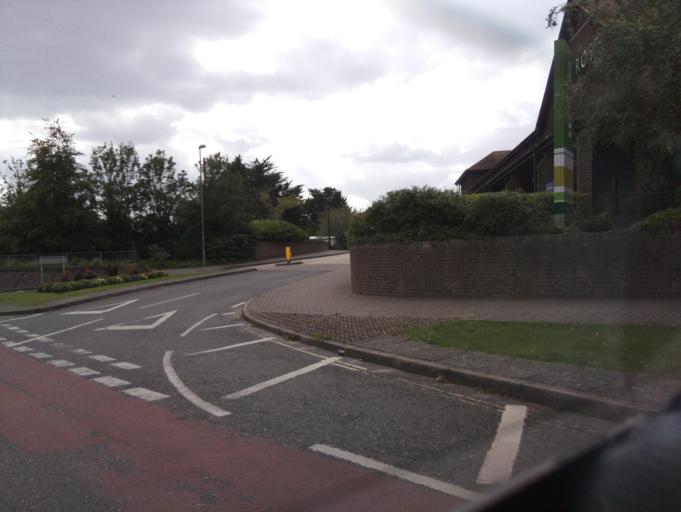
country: GB
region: England
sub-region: Hampshire
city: Lymington
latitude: 50.7575
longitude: -1.5494
